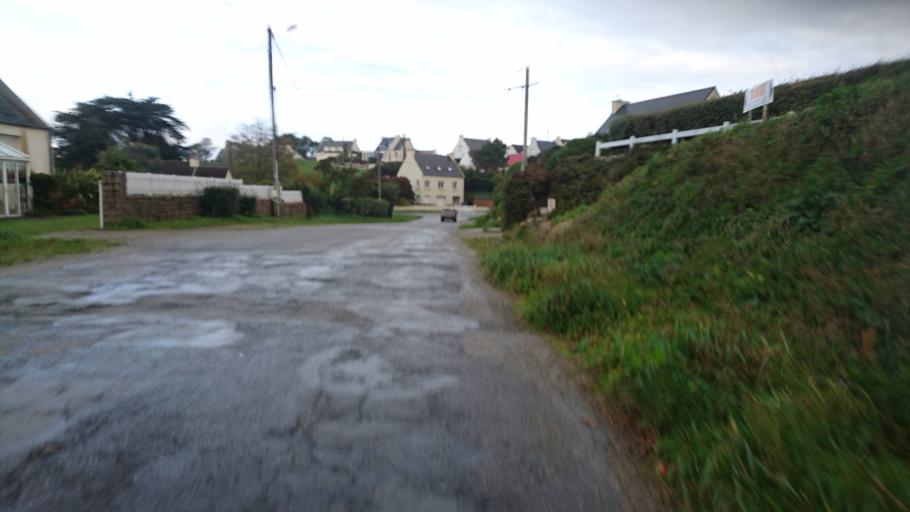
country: FR
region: Brittany
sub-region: Departement du Finistere
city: Lampaul-Plouarzel
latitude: 48.4435
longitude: -4.7698
